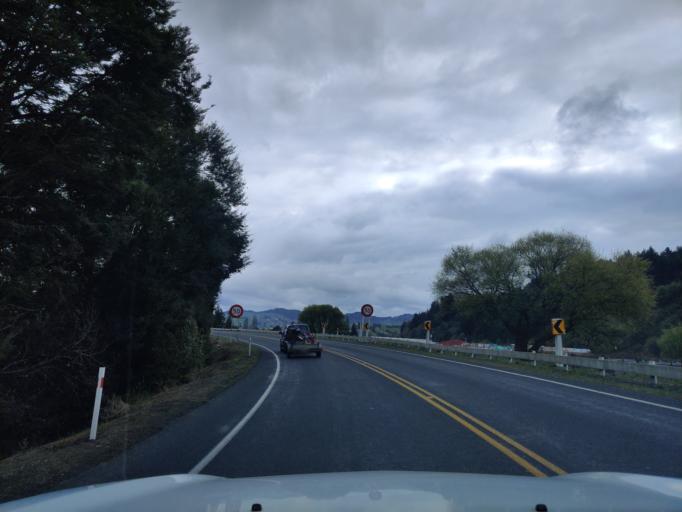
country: NZ
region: Waikato
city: Turangi
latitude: -38.8812
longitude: 175.2774
